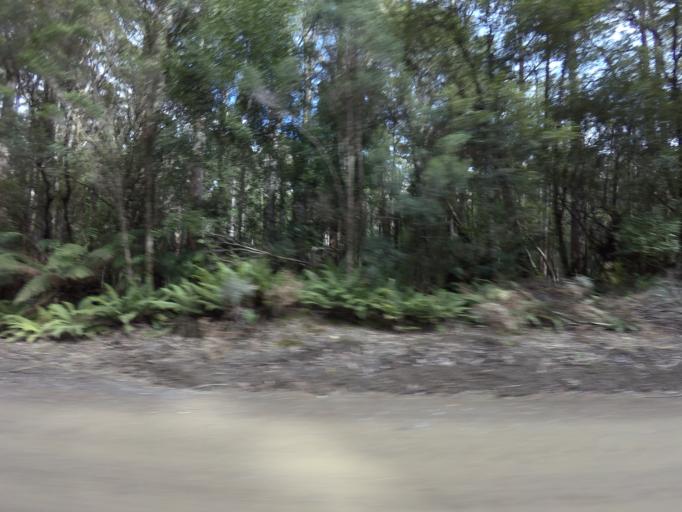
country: AU
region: Tasmania
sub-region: Huon Valley
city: Geeveston
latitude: -43.3920
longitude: 146.8540
